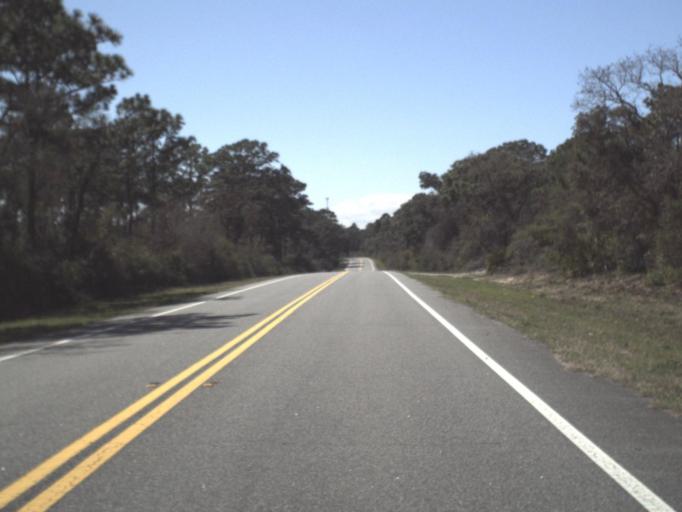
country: US
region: Florida
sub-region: Franklin County
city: Carrabelle
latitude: 29.9328
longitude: -84.4502
